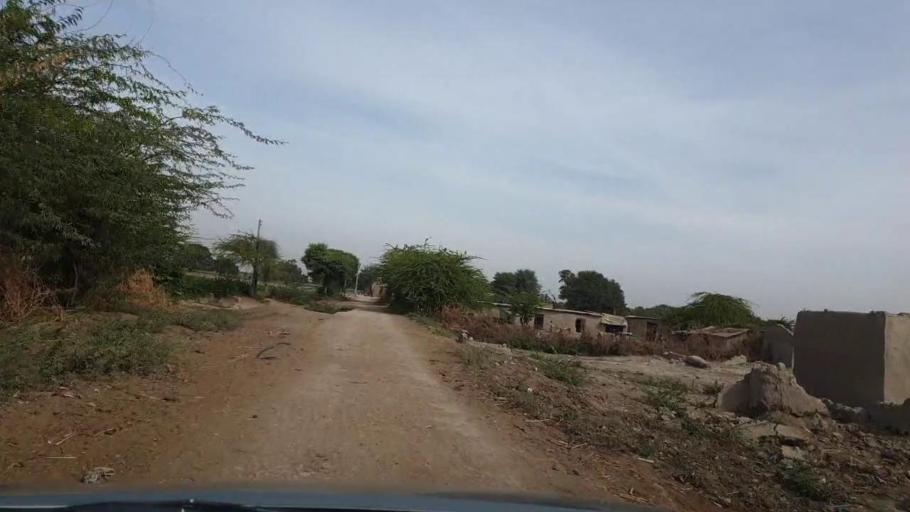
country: PK
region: Sindh
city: Kunri
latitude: 25.1654
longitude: 69.6224
